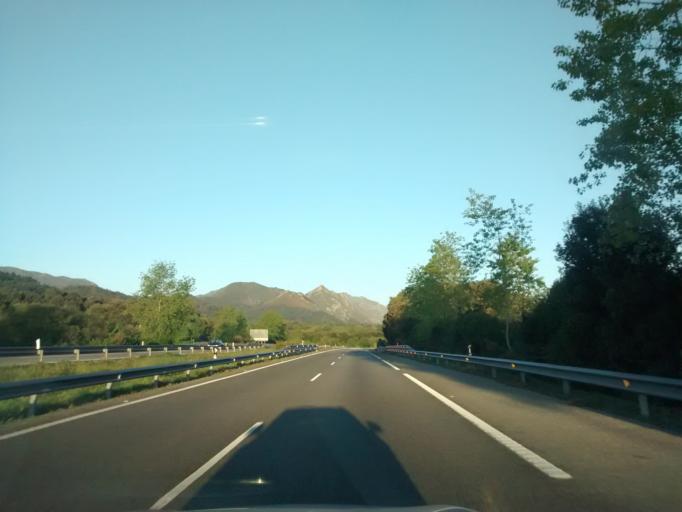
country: ES
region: Asturias
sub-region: Province of Asturias
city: Carrena
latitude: 43.4442
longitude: -4.9018
